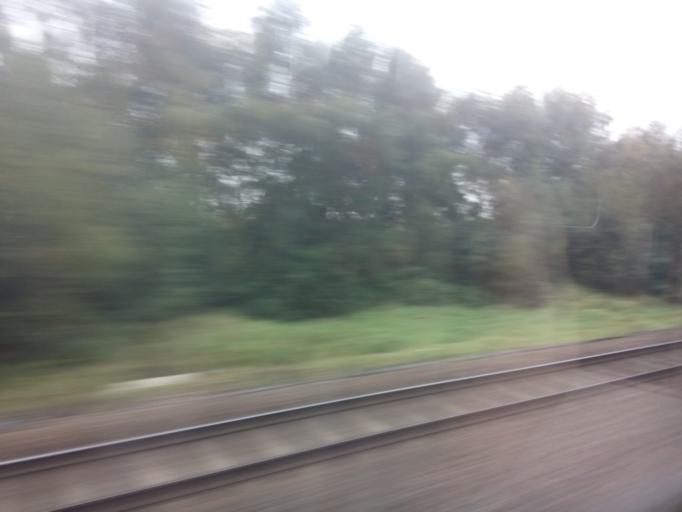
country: GB
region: England
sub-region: Kirklees
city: Mirfield
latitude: 53.6706
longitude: -1.6802
